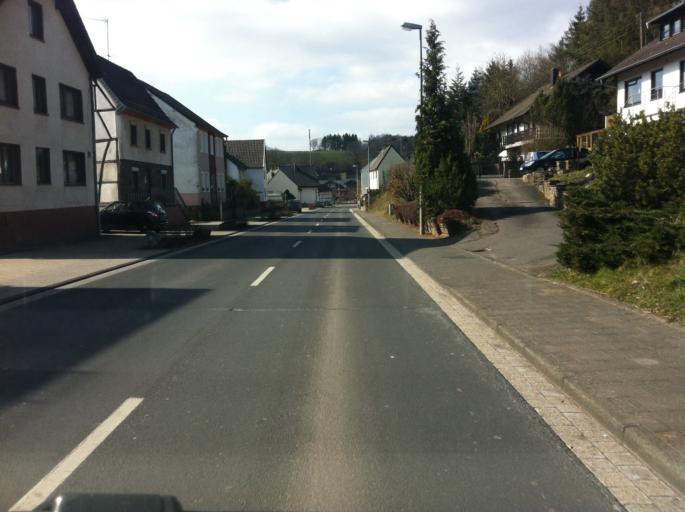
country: DE
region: North Rhine-Westphalia
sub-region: Regierungsbezirk Koln
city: Bad Munstereifel
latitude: 50.5323
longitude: 6.7732
